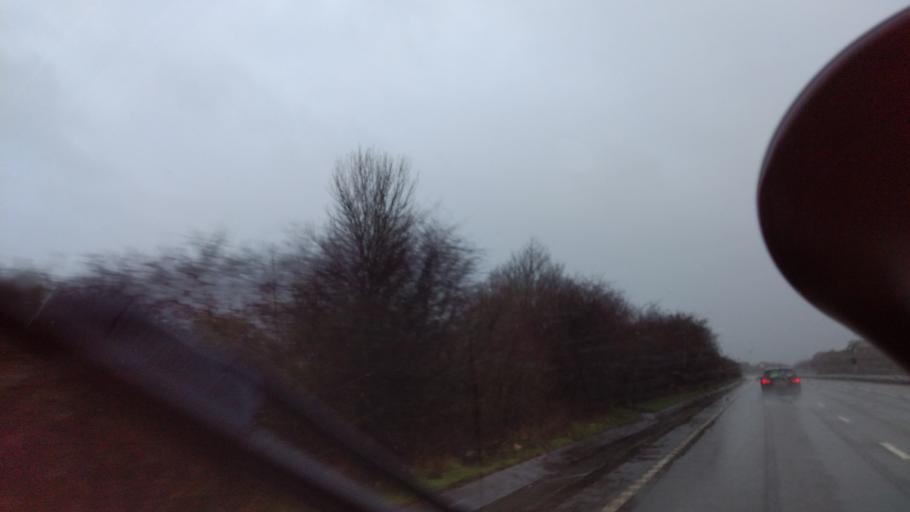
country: GB
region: England
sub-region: West Sussex
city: Rustington
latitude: 50.8399
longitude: -0.4693
